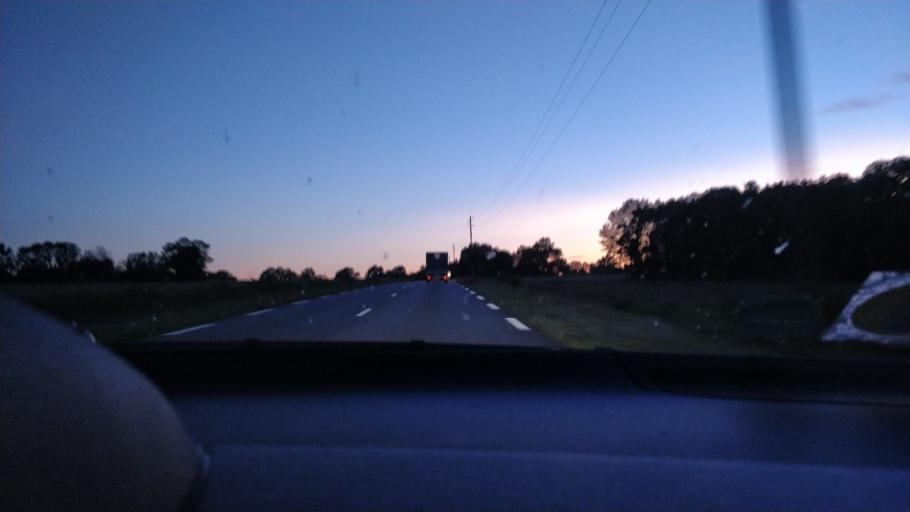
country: FR
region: Poitou-Charentes
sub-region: Departement de la Charente
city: Saint-Claud
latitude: 45.8616
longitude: 0.5281
